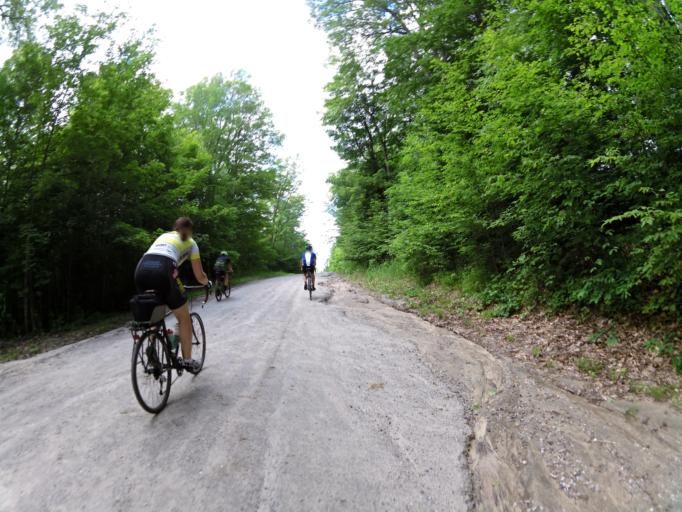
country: CA
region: Ontario
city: Perth
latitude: 45.0468
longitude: -76.4800
